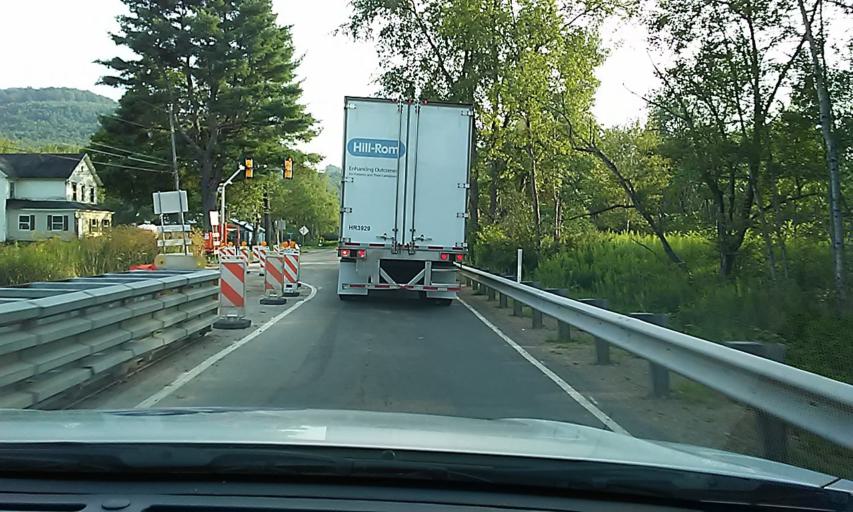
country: US
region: Pennsylvania
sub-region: McKean County
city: Smethport
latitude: 41.7498
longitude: -78.5266
